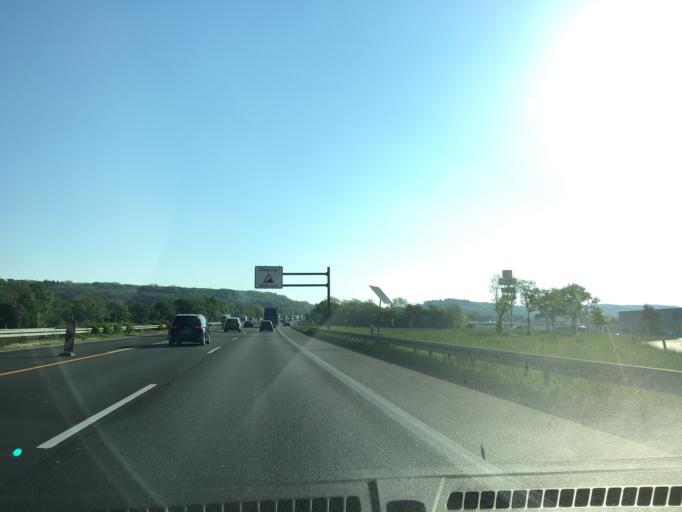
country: DE
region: North Rhine-Westphalia
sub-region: Regierungsbezirk Munster
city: Tecklenburg
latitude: 52.2010
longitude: 7.8091
